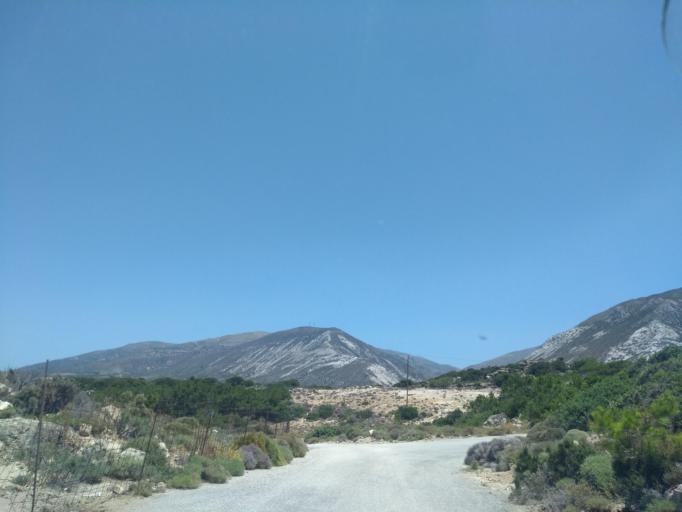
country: GR
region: Crete
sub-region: Nomos Chanias
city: Vryses
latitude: 35.3131
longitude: 23.5362
